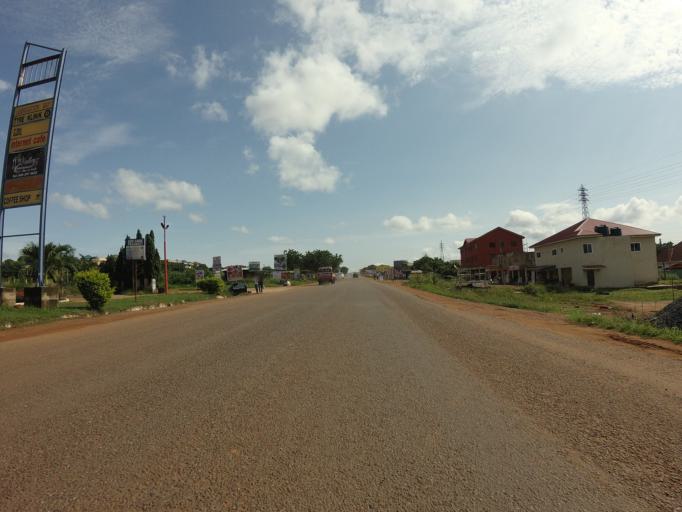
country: GH
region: Eastern
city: Aburi
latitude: 5.8105
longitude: -0.1233
